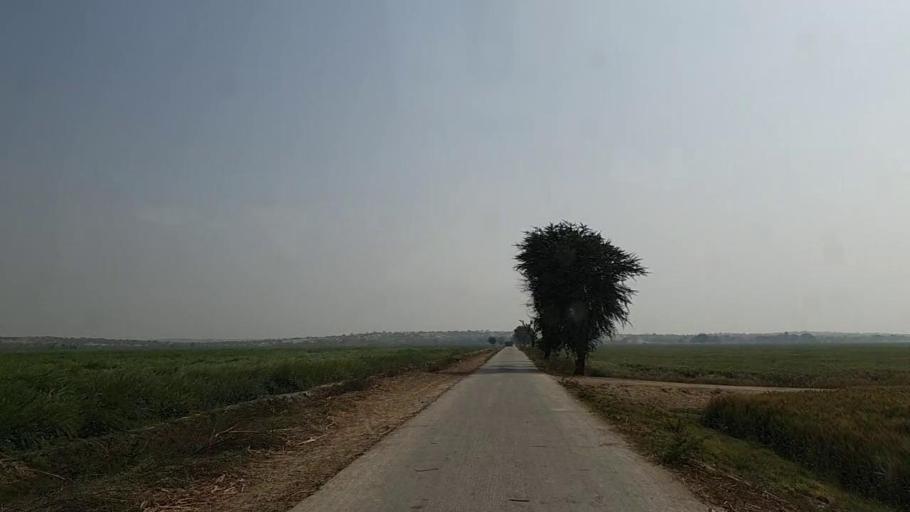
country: PK
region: Sindh
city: Naukot
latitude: 24.7550
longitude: 69.3472
